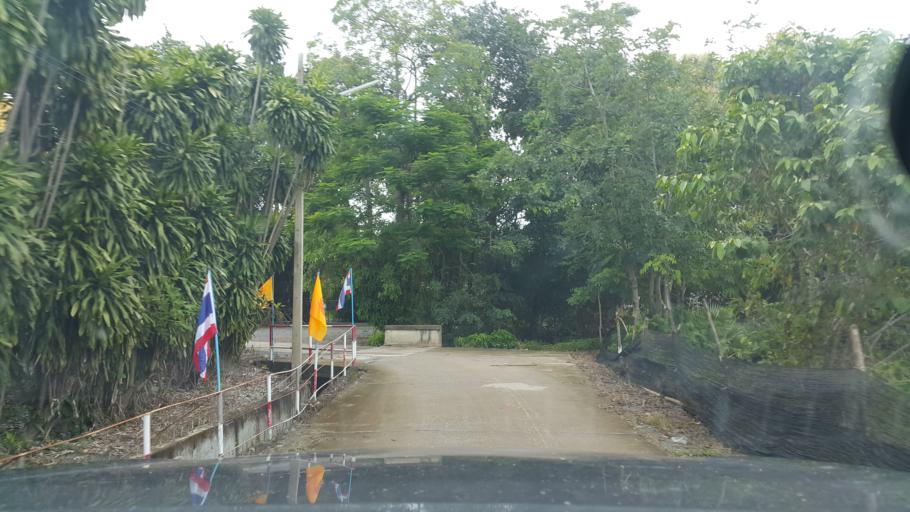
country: TH
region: Chiang Mai
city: Mae On
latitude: 18.8338
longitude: 99.1829
